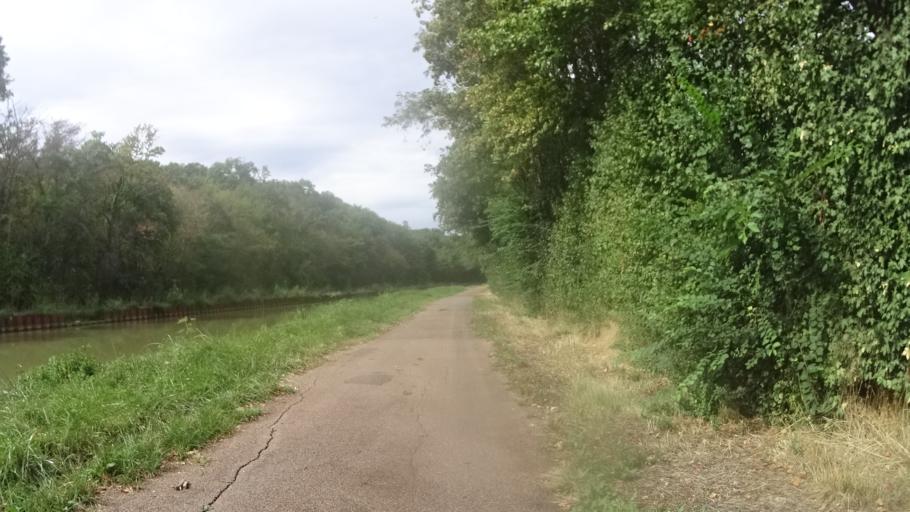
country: FR
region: Bourgogne
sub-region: Departement de la Nievre
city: Sermoise-sur-Loire
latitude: 46.9399
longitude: 3.2019
